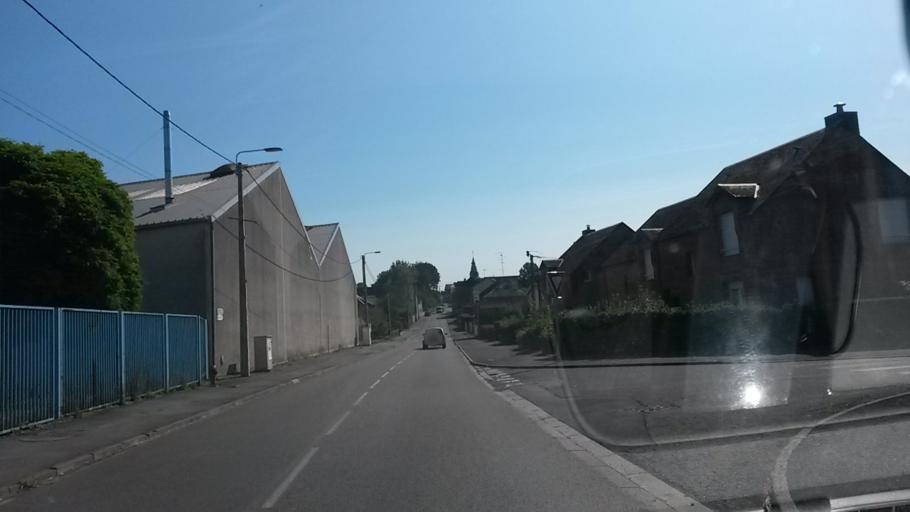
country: FR
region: Nord-Pas-de-Calais
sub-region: Departement du Nord
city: Avesnelles
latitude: 50.1191
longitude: 3.9412
